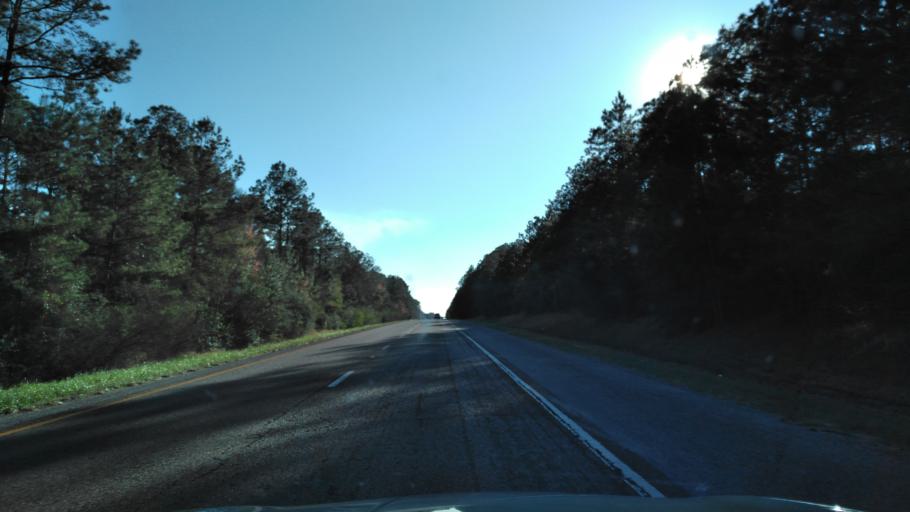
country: US
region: Alabama
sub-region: Baldwin County
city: Bay Minette
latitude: 31.0061
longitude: -87.6773
